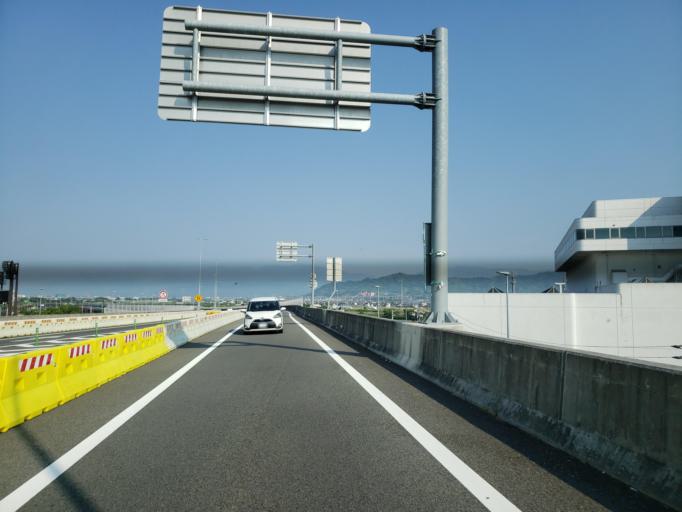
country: JP
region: Ehime
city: Masaki-cho
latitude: 33.8081
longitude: 132.7382
